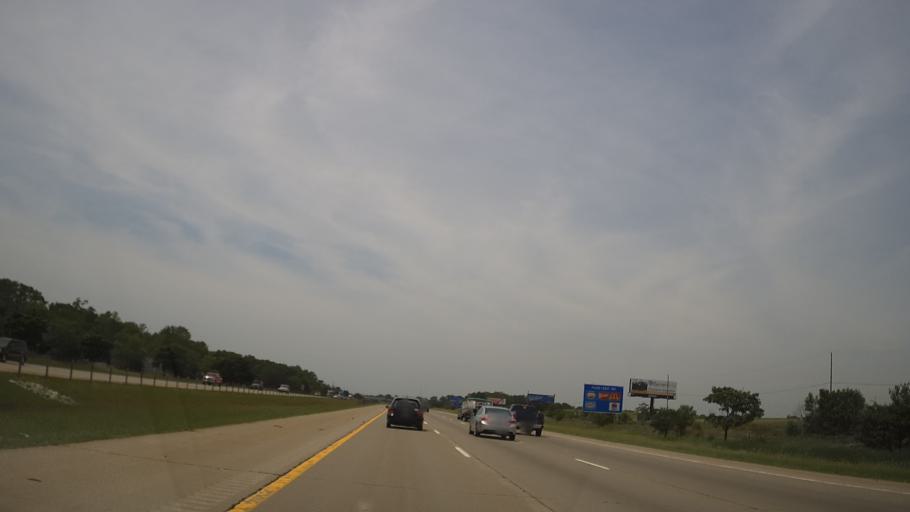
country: US
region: Michigan
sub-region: Wayne County
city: Belleville
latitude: 42.2189
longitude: -83.5269
